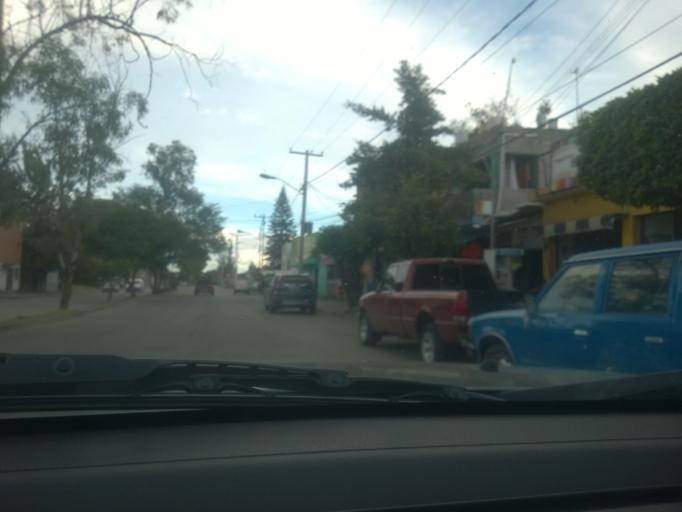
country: MX
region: Guanajuato
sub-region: Leon
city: Medina
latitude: 21.1307
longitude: -101.6417
